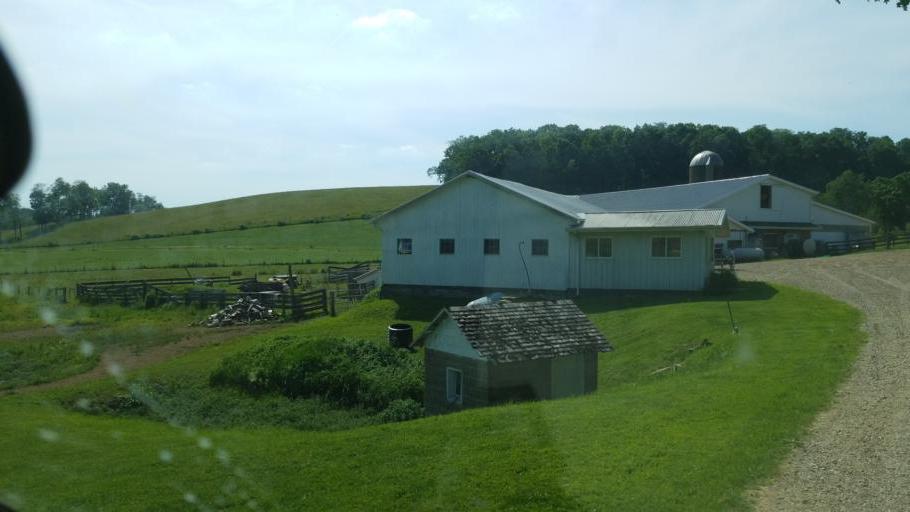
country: US
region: Ohio
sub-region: Ashland County
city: Loudonville
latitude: 40.5532
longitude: -82.3198
